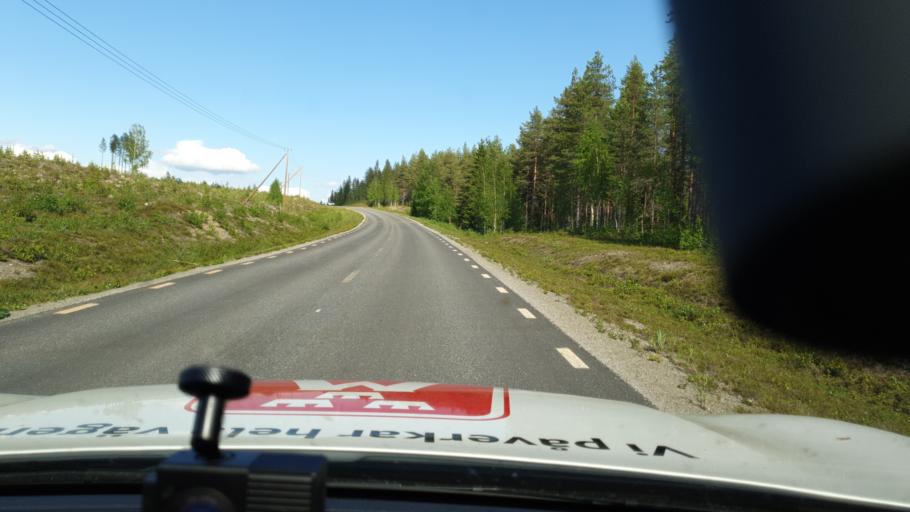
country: SE
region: Vaesterbotten
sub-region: Lycksele Kommun
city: Soderfors
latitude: 64.8774
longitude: 18.1396
